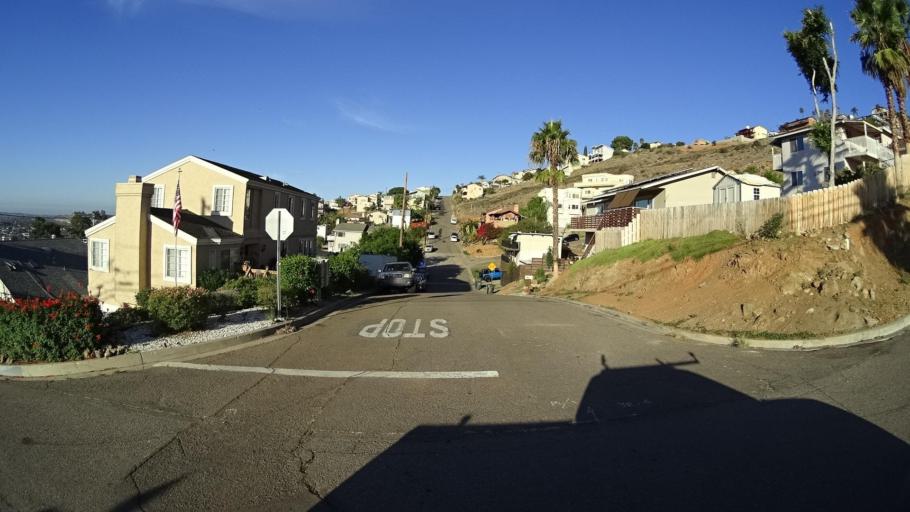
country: US
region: California
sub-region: San Diego County
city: La Presa
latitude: 32.7184
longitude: -116.9912
